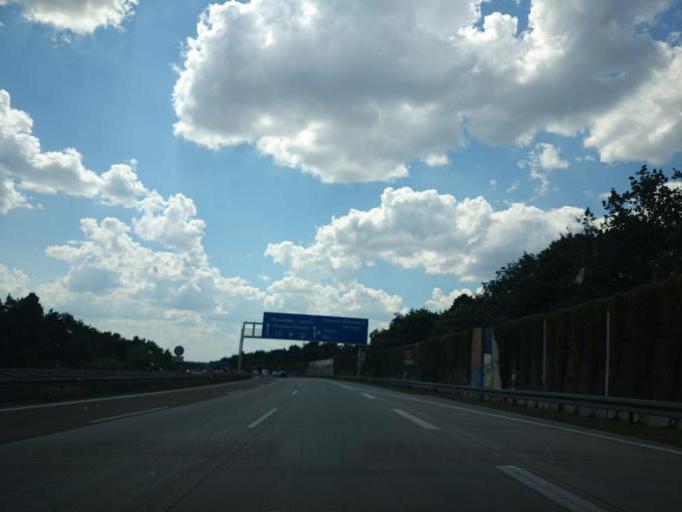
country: DE
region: Berlin
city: Wannsee
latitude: 52.3810
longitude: 13.1503
